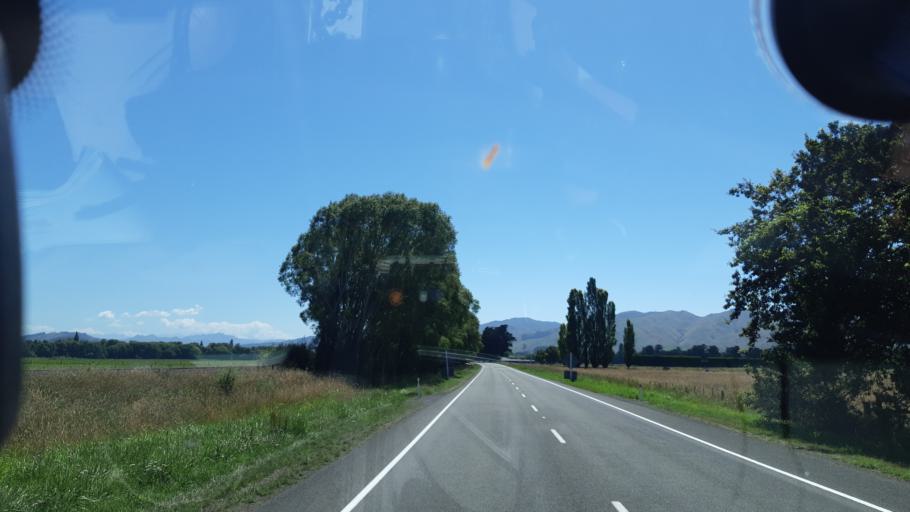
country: NZ
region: Canterbury
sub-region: Kaikoura District
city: Kaikoura
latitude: -42.7380
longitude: 173.2679
